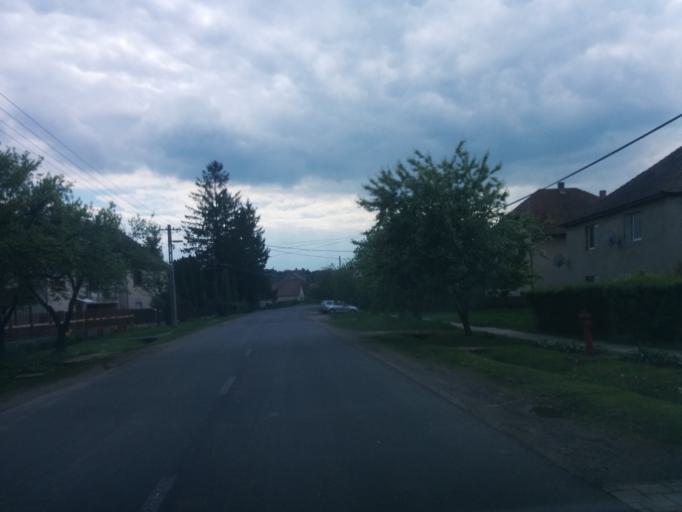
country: HU
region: Nograd
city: Romhany
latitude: 47.8436
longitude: 19.3024
